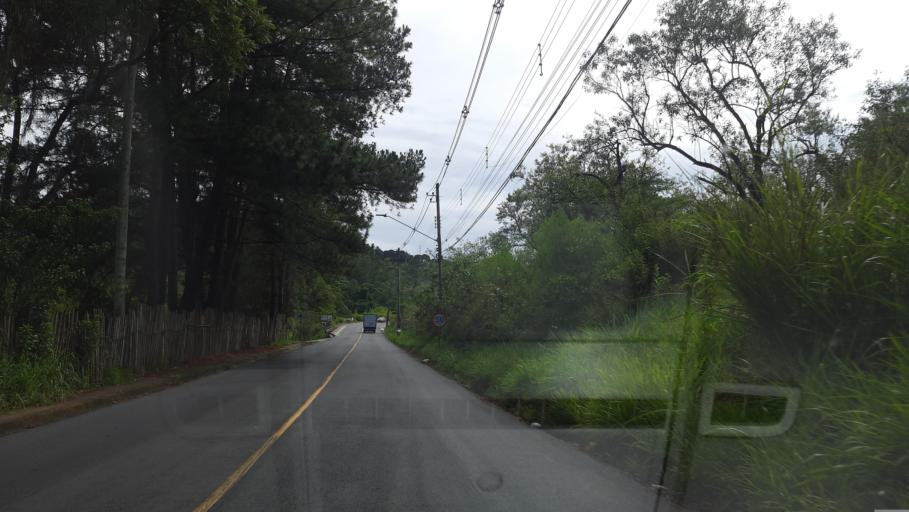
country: BR
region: Sao Paulo
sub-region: Caieiras
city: Caieiras
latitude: -23.3745
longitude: -46.6974
